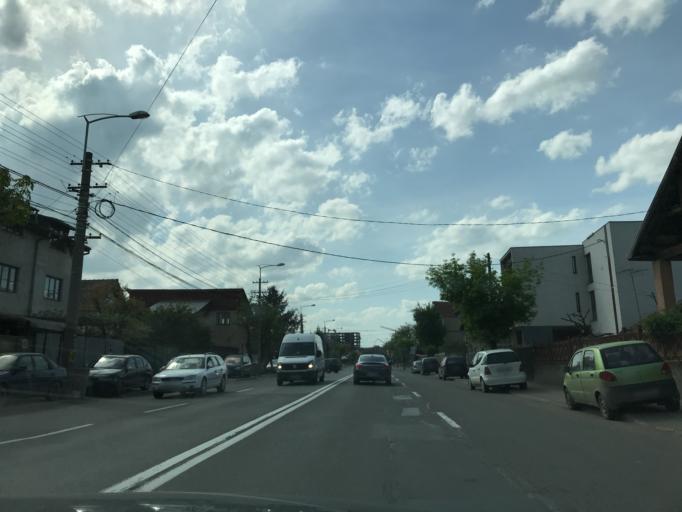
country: RO
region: Cluj
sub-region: Municipiul Cluj-Napoca
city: Cluj-Napoca
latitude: 46.7881
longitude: 23.6224
